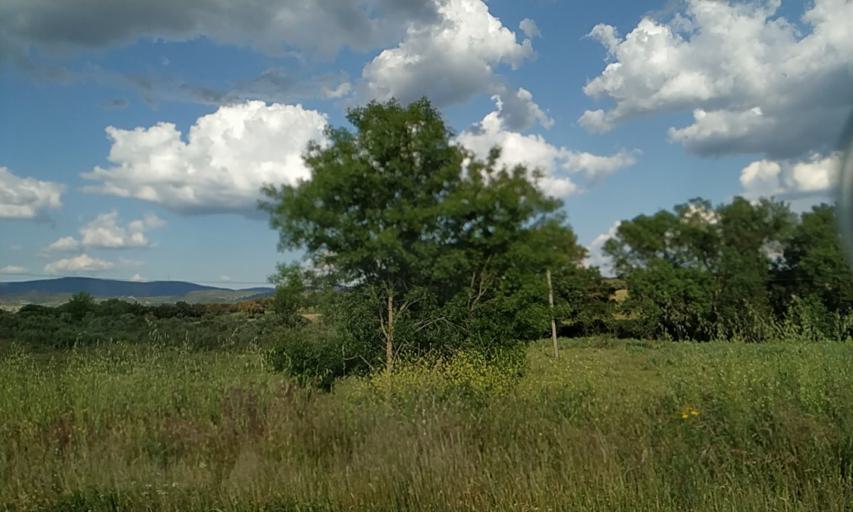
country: PT
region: Portalegre
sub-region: Portalegre
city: Portalegre
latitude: 39.2489
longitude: -7.4488
